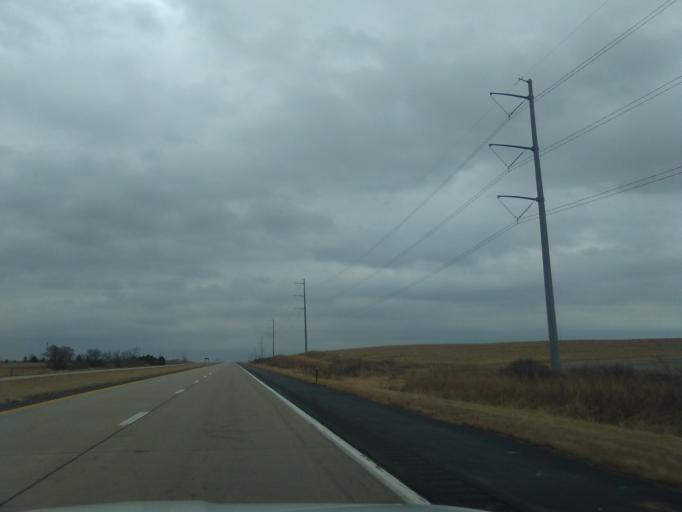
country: US
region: Nebraska
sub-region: Otoe County
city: Syracuse
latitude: 40.6681
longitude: -96.1472
